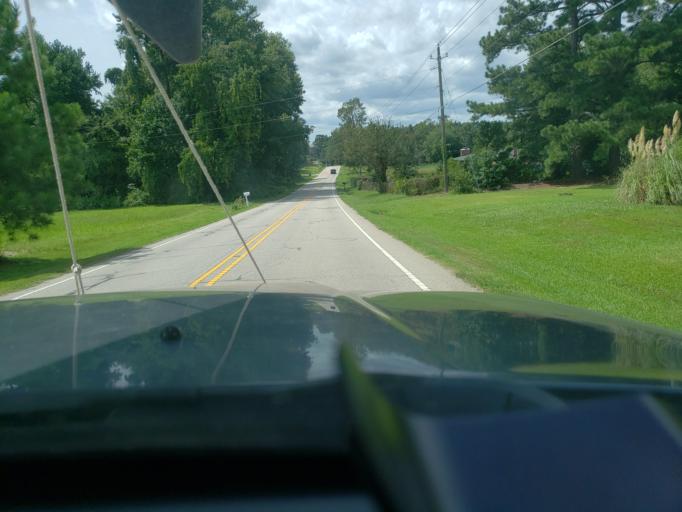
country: US
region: North Carolina
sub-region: Wake County
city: Rolesville
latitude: 35.8779
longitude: -78.4542
